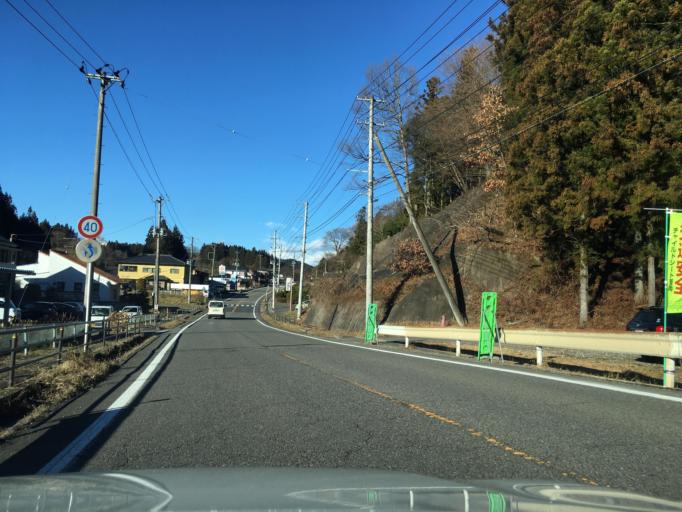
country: JP
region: Fukushima
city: Funehikimachi-funehiki
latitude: 37.2817
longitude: 140.6348
